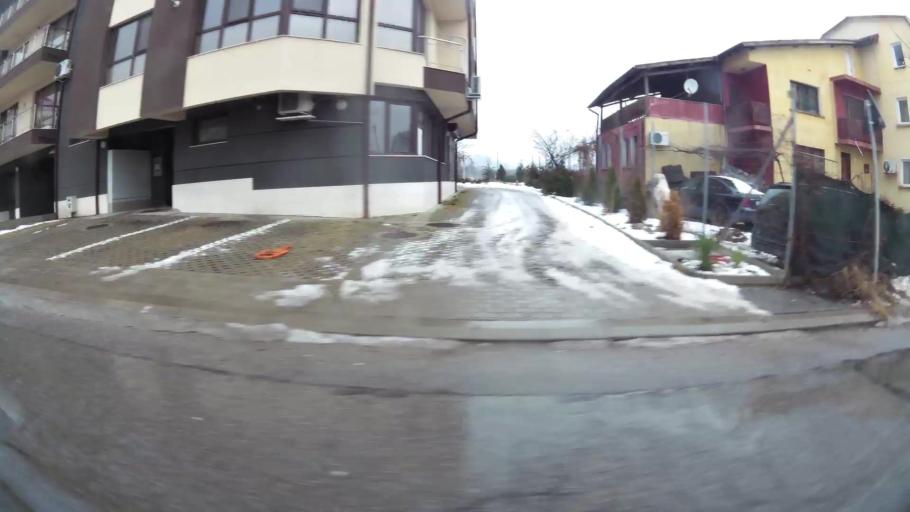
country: BG
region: Sofia-Capital
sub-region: Stolichna Obshtina
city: Sofia
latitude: 42.6566
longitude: 23.2978
